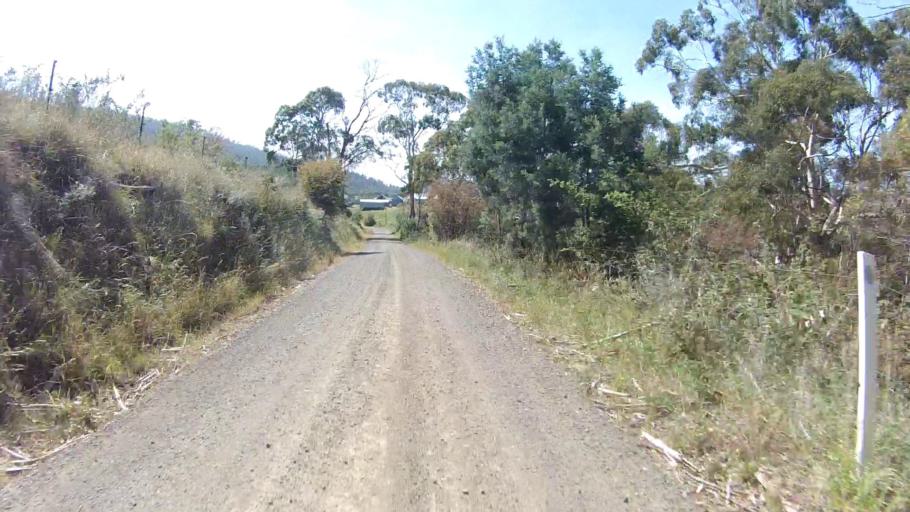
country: AU
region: Tasmania
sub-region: Sorell
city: Sorell
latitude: -42.7470
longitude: 147.6122
